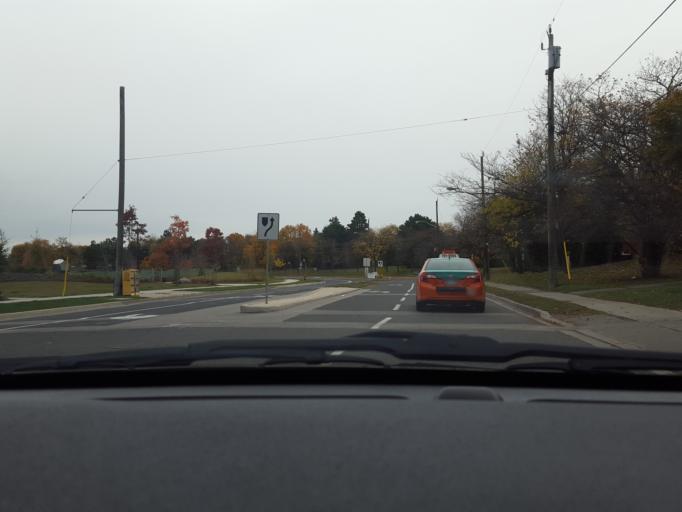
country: CA
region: Ontario
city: Willowdale
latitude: 43.7327
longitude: -79.3464
